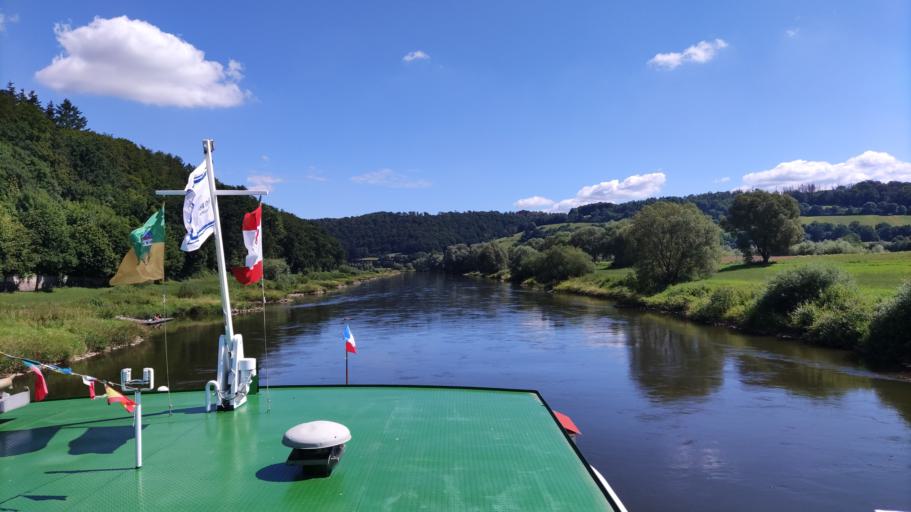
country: DE
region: North Rhine-Westphalia
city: Beverungen
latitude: 51.6923
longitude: 9.3896
